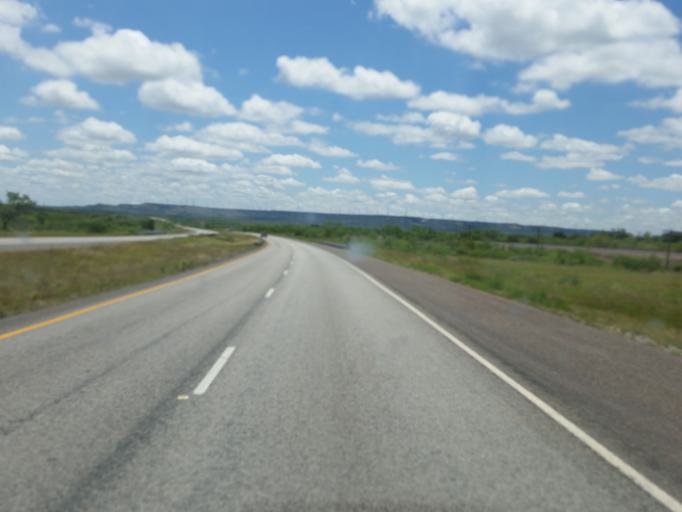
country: US
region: Texas
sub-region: Garza County
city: Post
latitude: 33.0158
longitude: -101.1777
